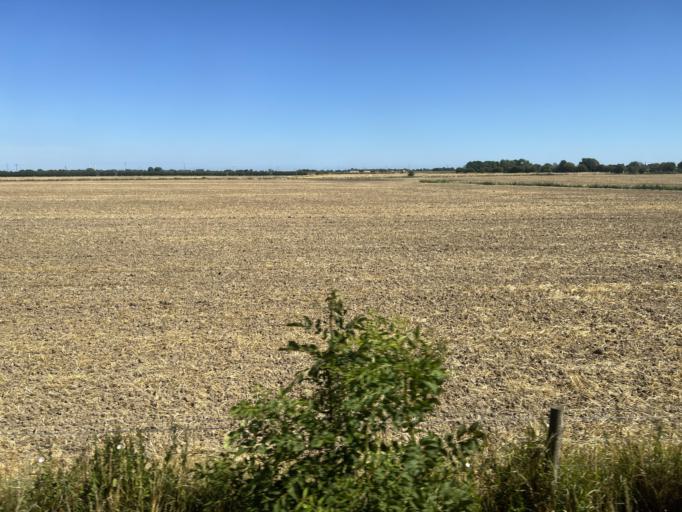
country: GB
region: England
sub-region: Lincolnshire
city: Wainfleet All Saints
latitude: 53.1113
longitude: 0.2214
